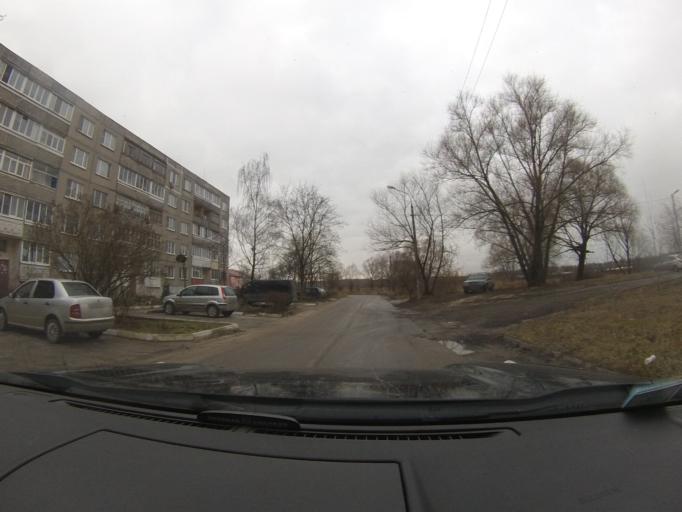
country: RU
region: Moskovskaya
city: Lopatinskiy
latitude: 55.3415
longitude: 38.7139
